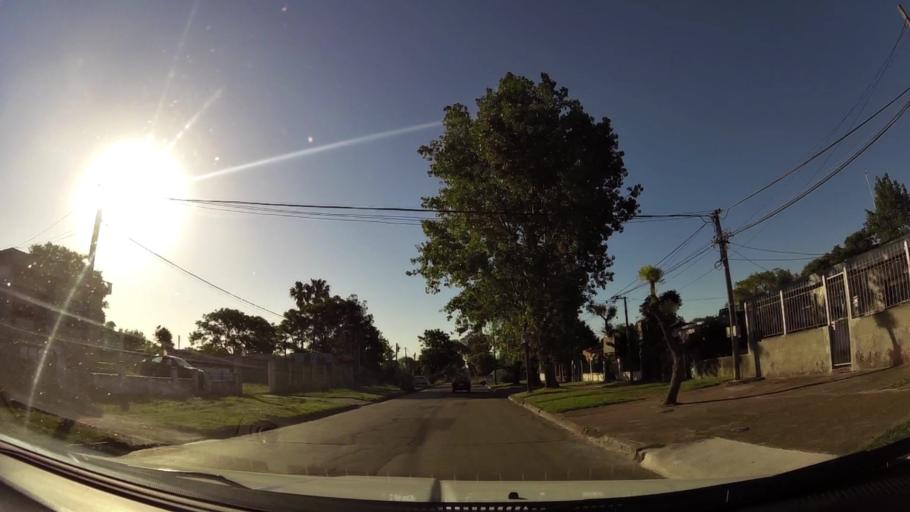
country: UY
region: Canelones
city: La Paz
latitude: -34.8363
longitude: -56.2337
